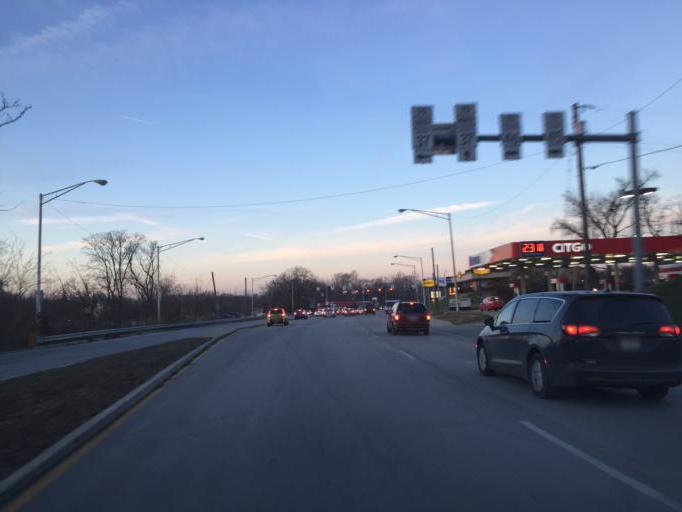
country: US
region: Indiana
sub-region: Monroe County
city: Bloomington
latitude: 39.1849
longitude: -86.5345
